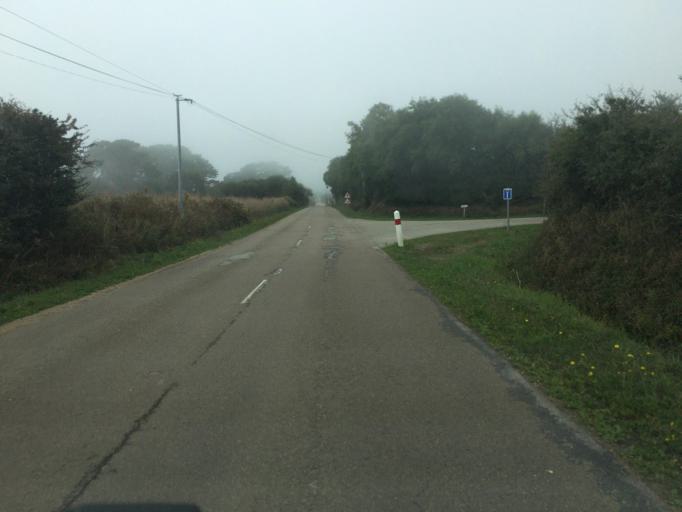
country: FR
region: Brittany
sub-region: Departement du Finistere
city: Plogoff
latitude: 48.0636
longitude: -4.6127
